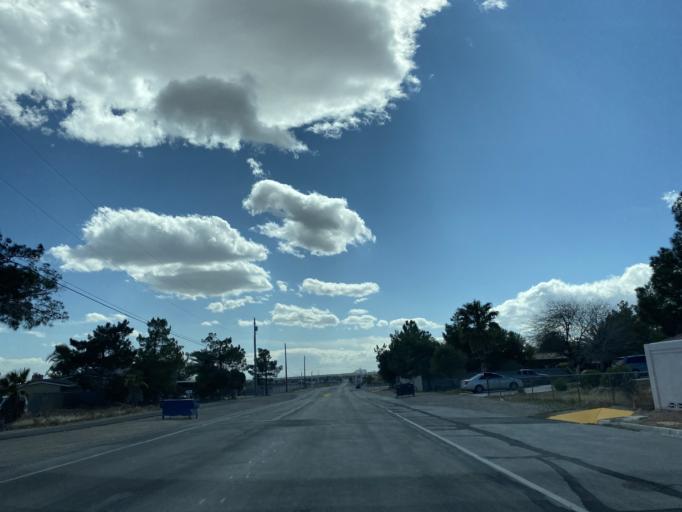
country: US
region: Nevada
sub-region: Clark County
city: Summerlin South
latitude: 36.2513
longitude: -115.2884
